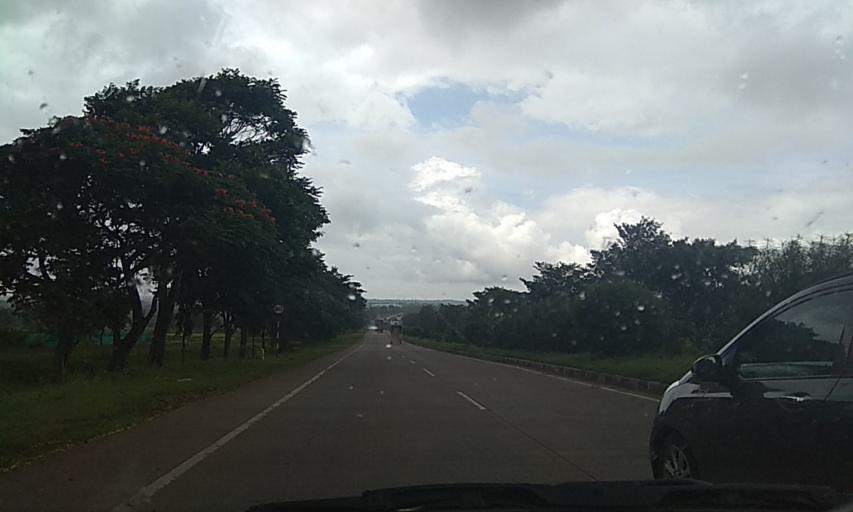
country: IN
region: Karnataka
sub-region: Belgaum
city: Sankeshwar
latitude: 16.2900
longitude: 74.4415
